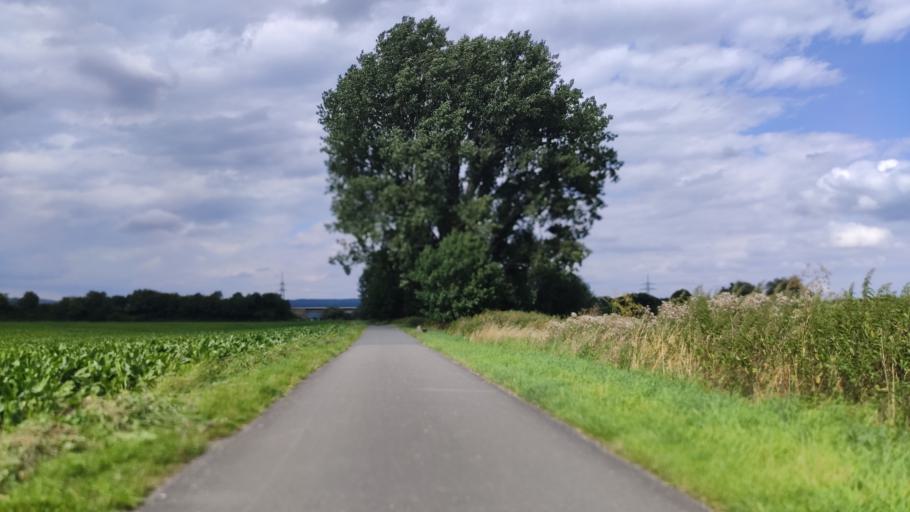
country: DE
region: North Rhine-Westphalia
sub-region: Regierungsbezirk Detmold
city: Hoexter
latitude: 51.7946
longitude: 9.4188
